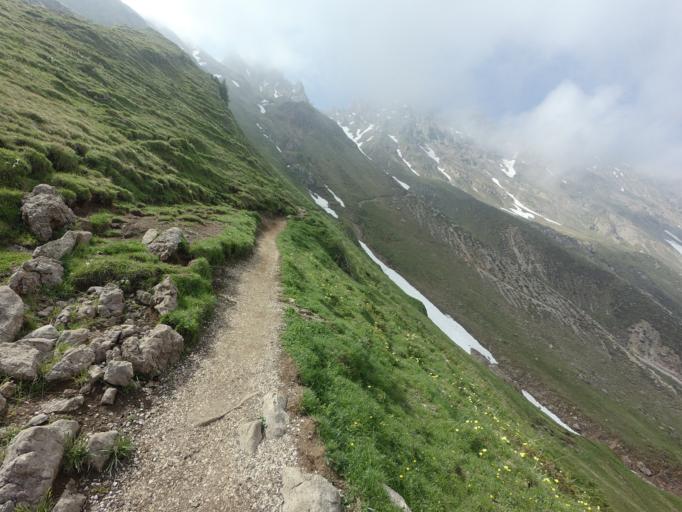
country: IT
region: Trentino-Alto Adige
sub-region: Bolzano
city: Ortisei
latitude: 46.5076
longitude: 11.6351
